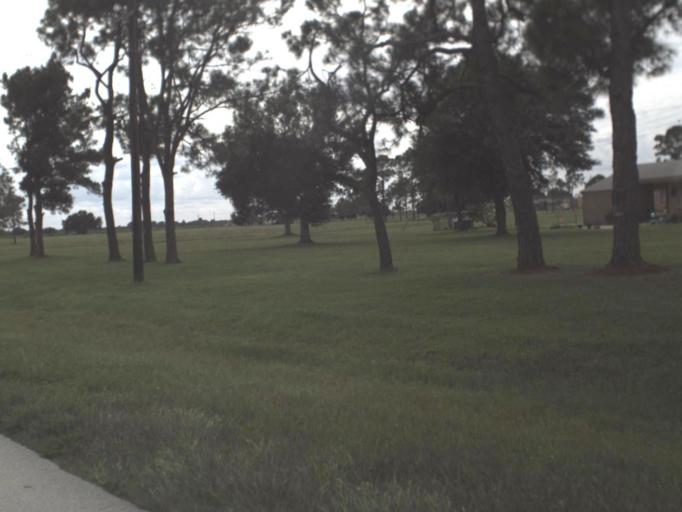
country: US
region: Florida
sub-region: DeSoto County
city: Southeast Arcadia
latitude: 27.1381
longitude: -81.7964
